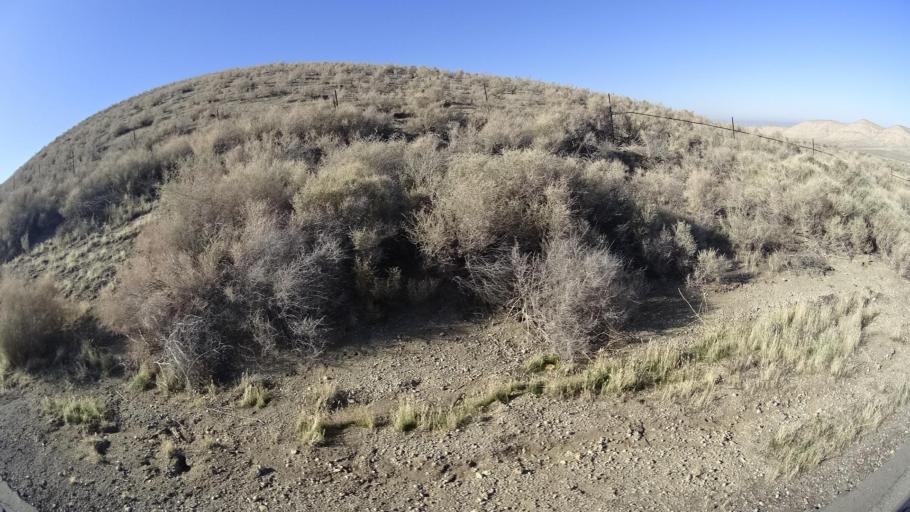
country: US
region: California
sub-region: Kern County
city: Maricopa
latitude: 34.9858
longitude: -119.3932
